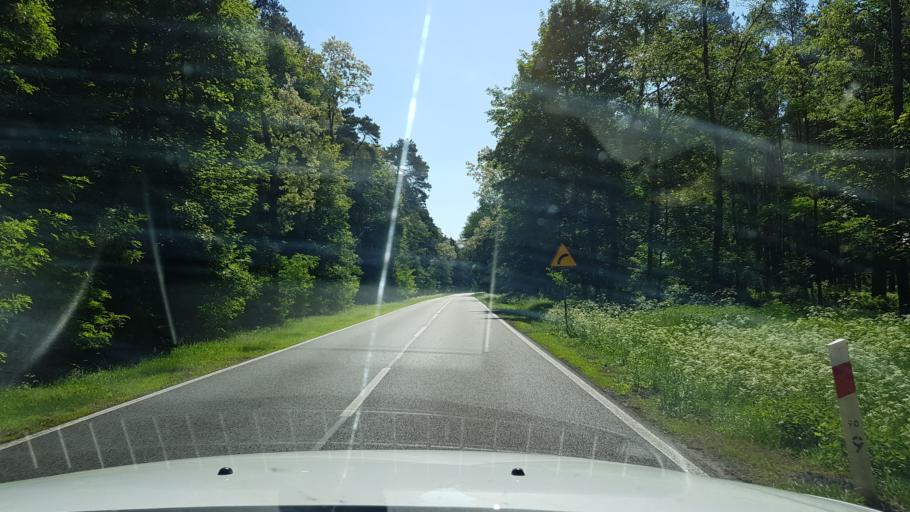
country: PL
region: West Pomeranian Voivodeship
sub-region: Powiat mysliborski
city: Boleszkowice
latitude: 52.7044
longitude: 14.5990
